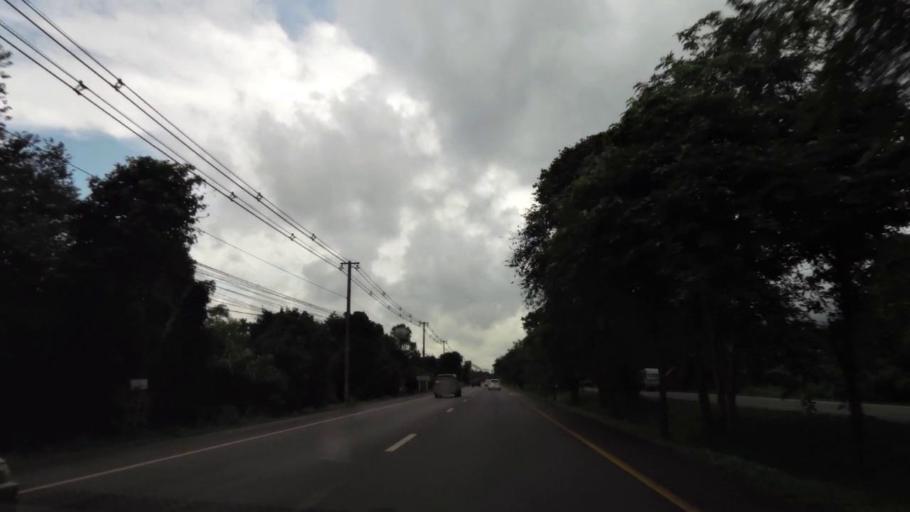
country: TH
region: Chanthaburi
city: Khlung
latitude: 12.4991
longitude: 102.1713
